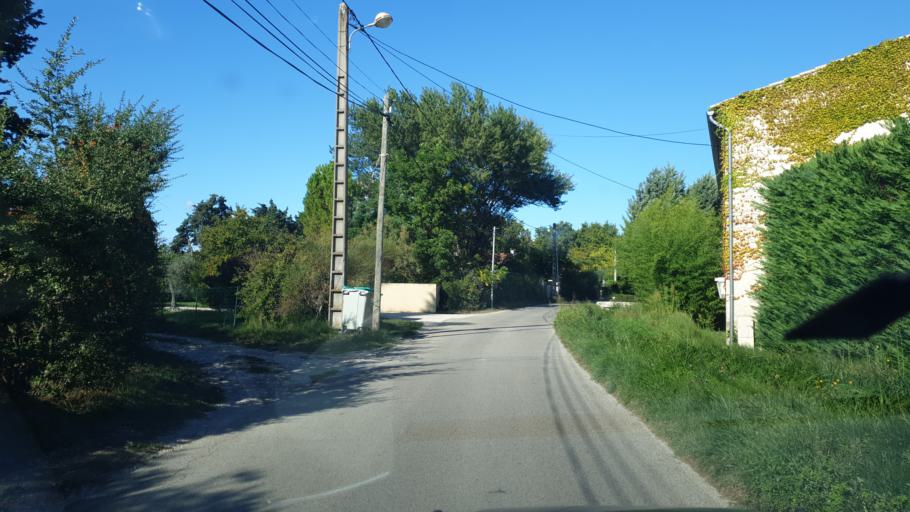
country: FR
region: Provence-Alpes-Cote d'Azur
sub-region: Departement du Vaucluse
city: Monteux
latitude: 44.0427
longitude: 5.0035
